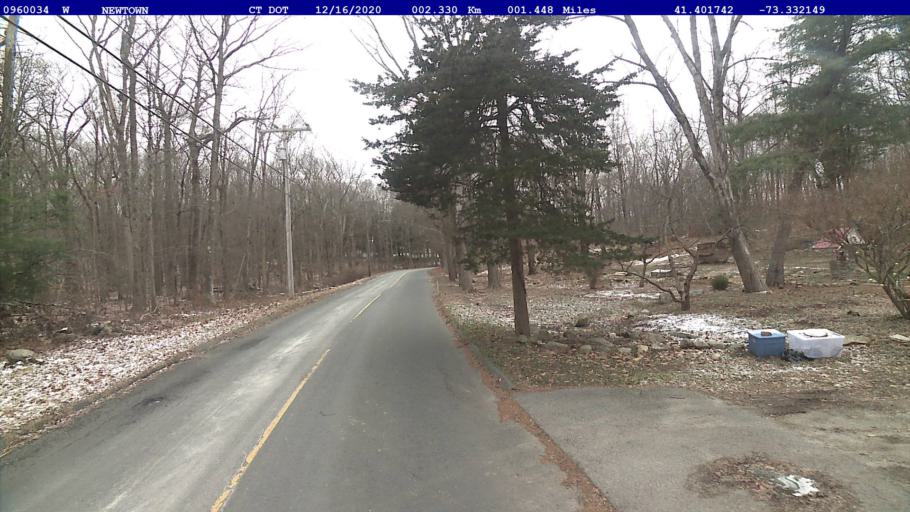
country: US
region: Connecticut
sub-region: Fairfield County
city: Newtown
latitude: 41.4017
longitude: -73.3322
